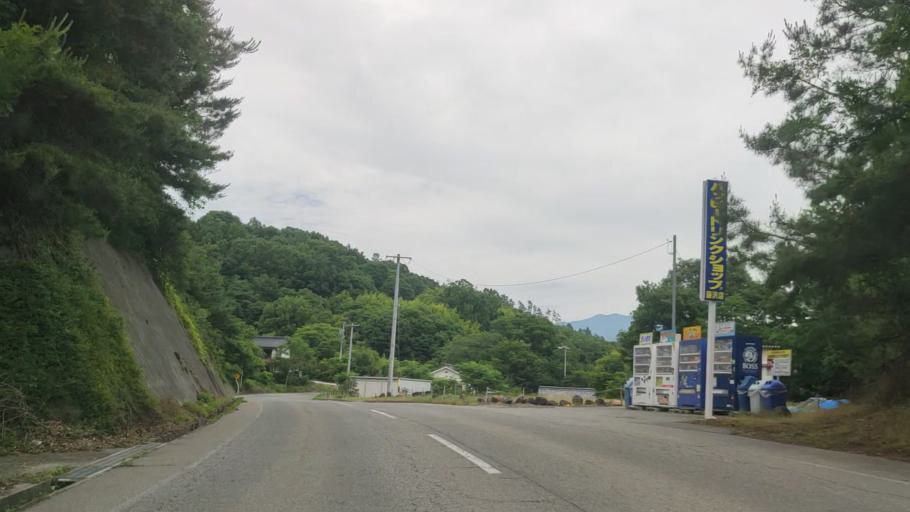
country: JP
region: Nagano
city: Kamimaruko
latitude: 36.3100
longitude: 138.3287
